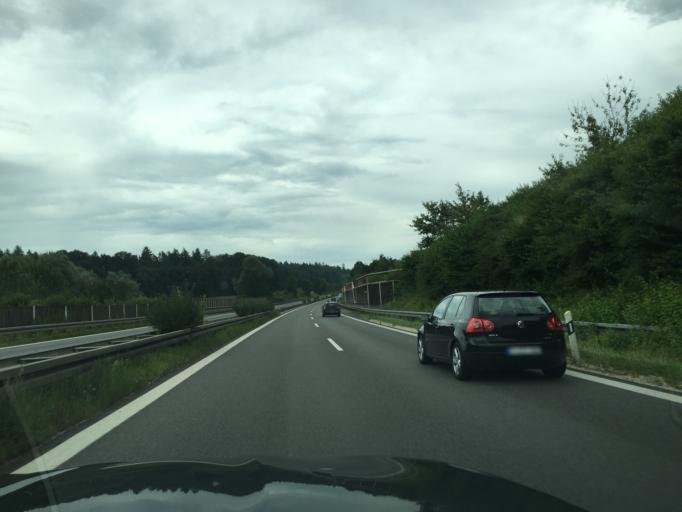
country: DE
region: Baden-Wuerttemberg
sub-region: Freiburg Region
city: Radolfzell am Bodensee
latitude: 47.7471
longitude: 9.0111
